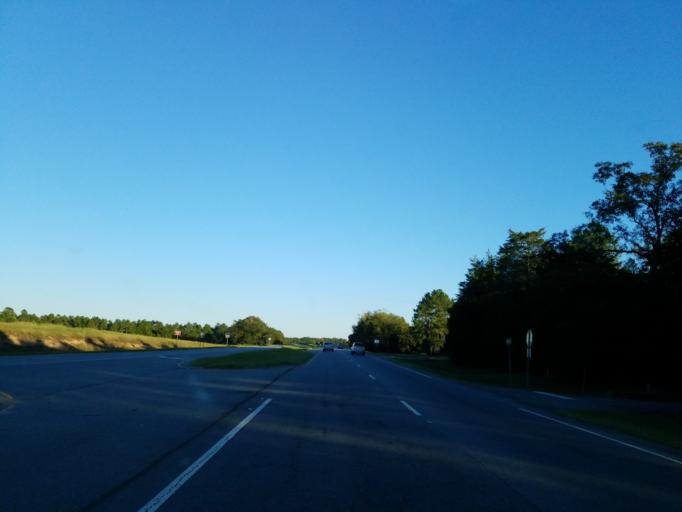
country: US
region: Georgia
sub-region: Worth County
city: Sylvester
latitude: 31.5154
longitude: -83.7811
